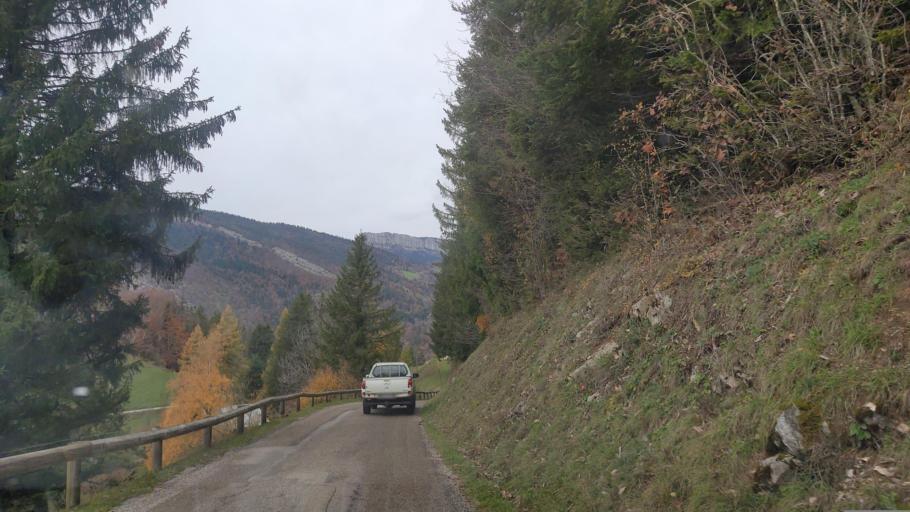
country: FR
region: Rhone-Alpes
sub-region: Departement de l'Isere
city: Saint-Vincent-de-Mercuze
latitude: 45.4164
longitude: 5.8717
